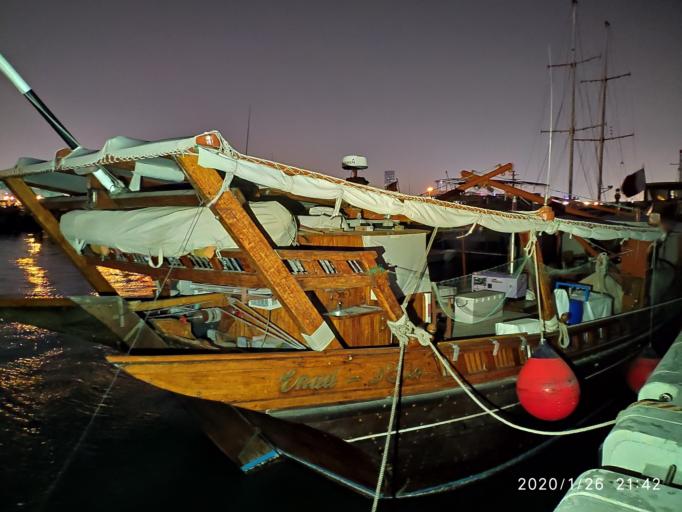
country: QA
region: Baladiyat ad Dawhah
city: Doha
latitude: 25.2946
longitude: 51.5369
